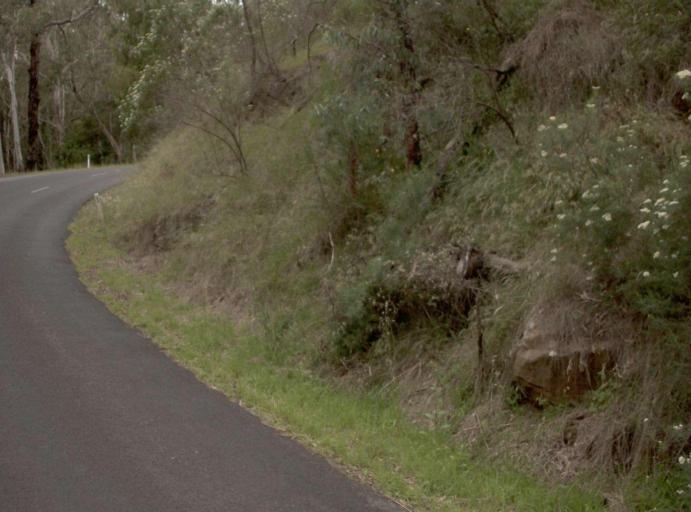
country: AU
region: Victoria
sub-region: East Gippsland
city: Bairnsdale
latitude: -37.4832
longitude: 147.2053
